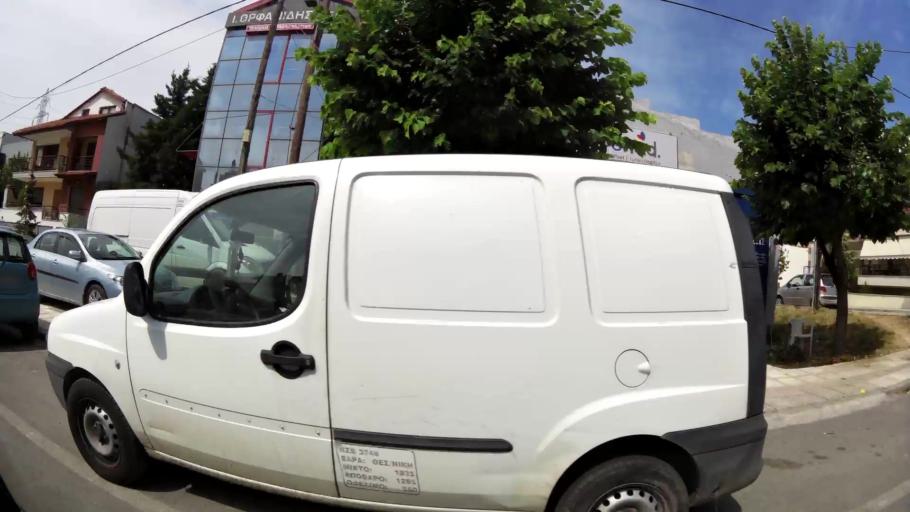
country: GR
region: Central Macedonia
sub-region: Nomos Thessalonikis
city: Pylaia
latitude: 40.5953
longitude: 22.9858
